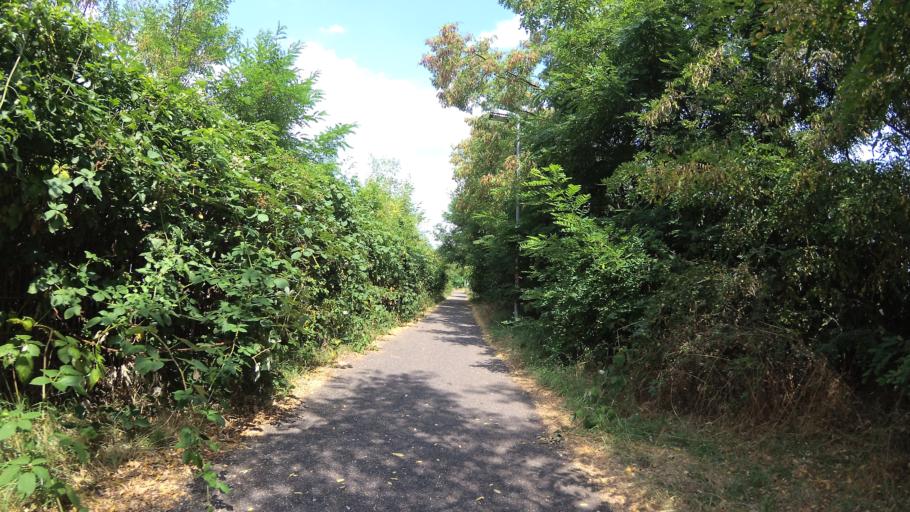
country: DE
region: Saarland
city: Saarbrucken
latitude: 49.2375
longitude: 6.9621
